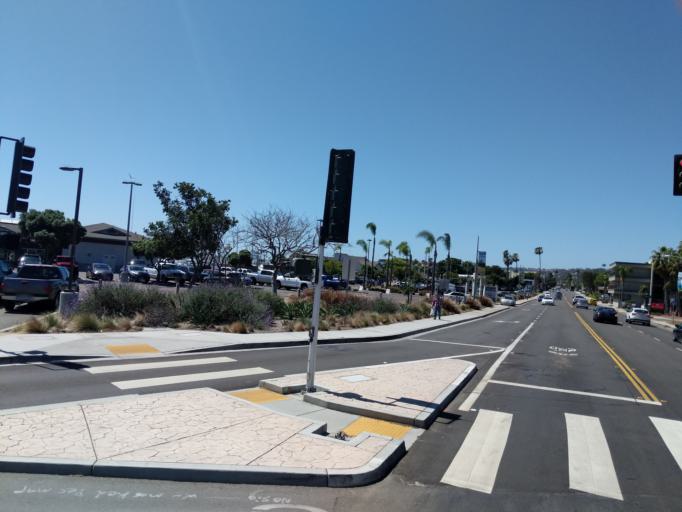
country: US
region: California
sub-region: San Diego County
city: Coronado
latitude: 32.7256
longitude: -117.2268
